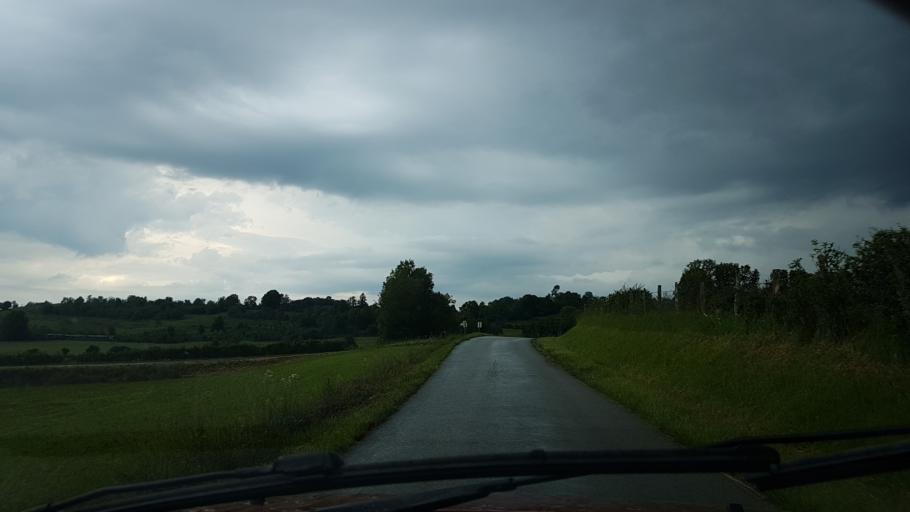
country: FR
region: Franche-Comte
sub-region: Departement du Jura
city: Clairvaux-les-Lacs
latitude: 46.5343
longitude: 5.7291
